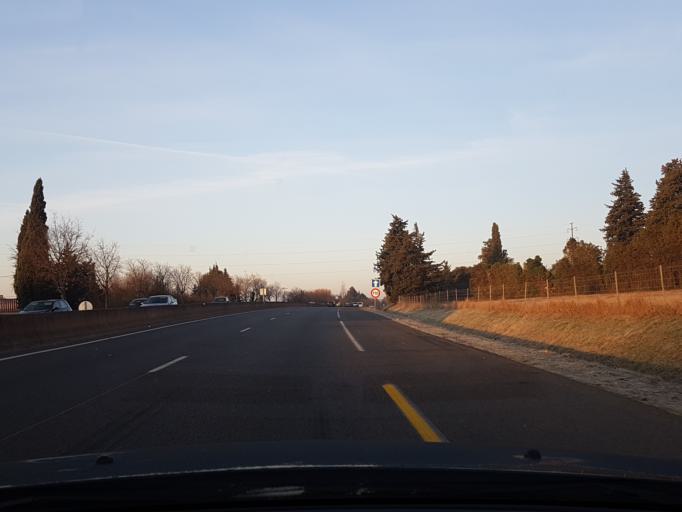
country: FR
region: Provence-Alpes-Cote d'Azur
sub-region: Departement du Vaucluse
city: Monteux
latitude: 44.0450
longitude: 5.0159
